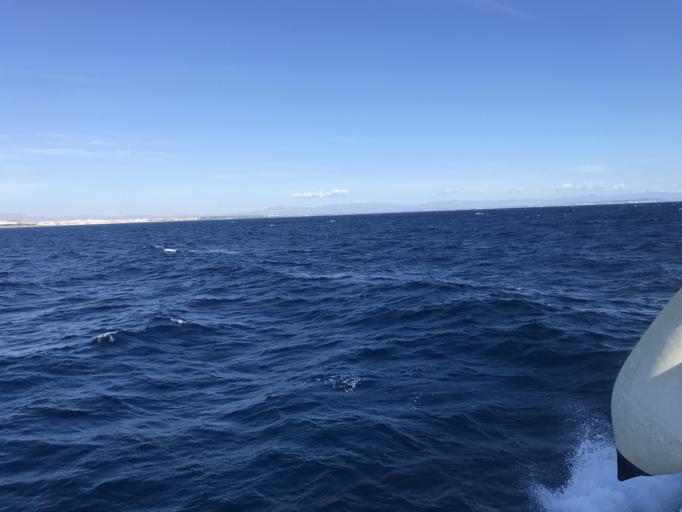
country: ES
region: Valencia
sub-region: Provincia de Alicante
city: Guardamar del Segura
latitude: 38.0311
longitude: -0.6146
